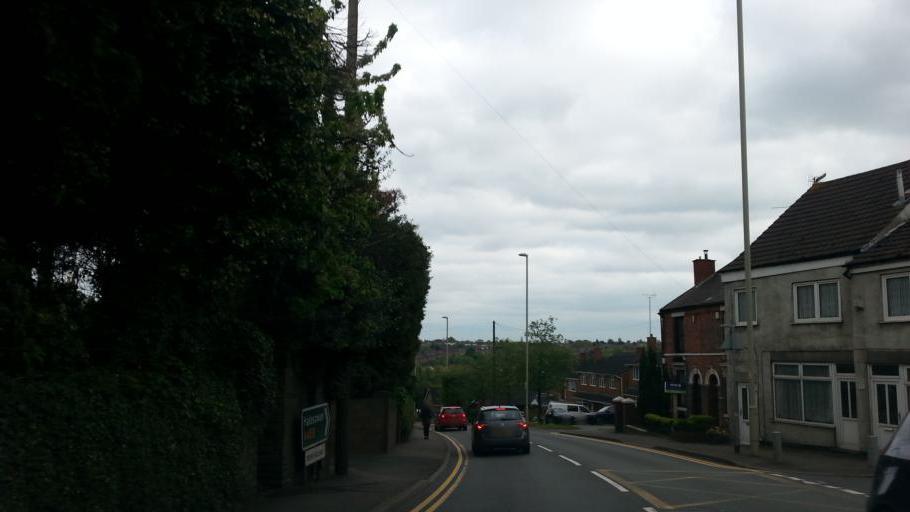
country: GB
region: England
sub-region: Sandwell
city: Cradley Heath
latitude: 52.4576
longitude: -2.0821
